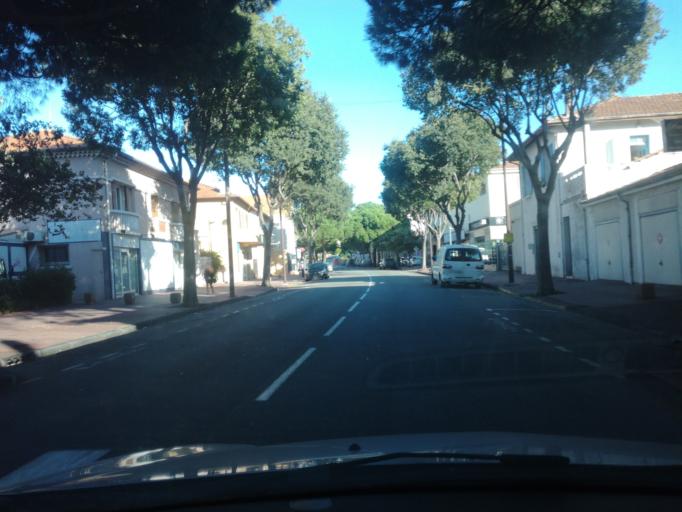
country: FR
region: Provence-Alpes-Cote d'Azur
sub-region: Departement du Var
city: Frejus
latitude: 43.4331
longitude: 6.7295
